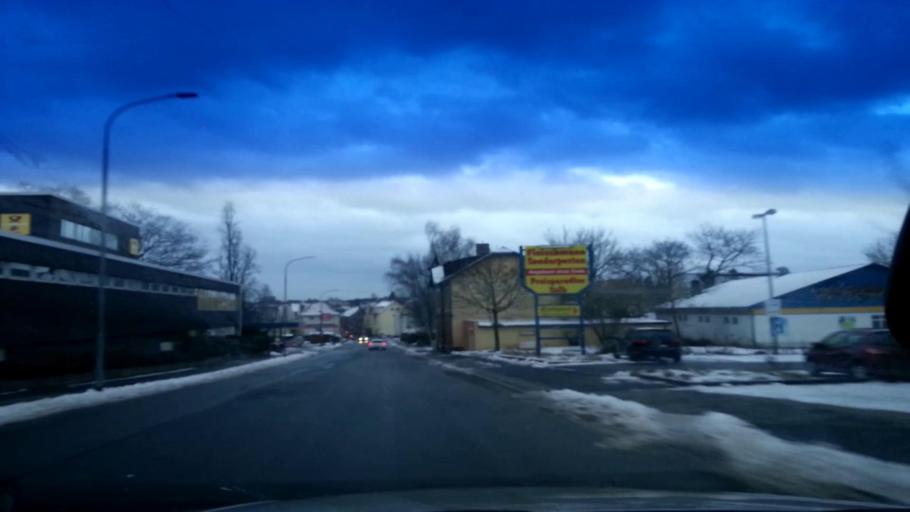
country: DE
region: Bavaria
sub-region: Upper Franconia
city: Selb
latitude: 50.1729
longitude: 12.1265
